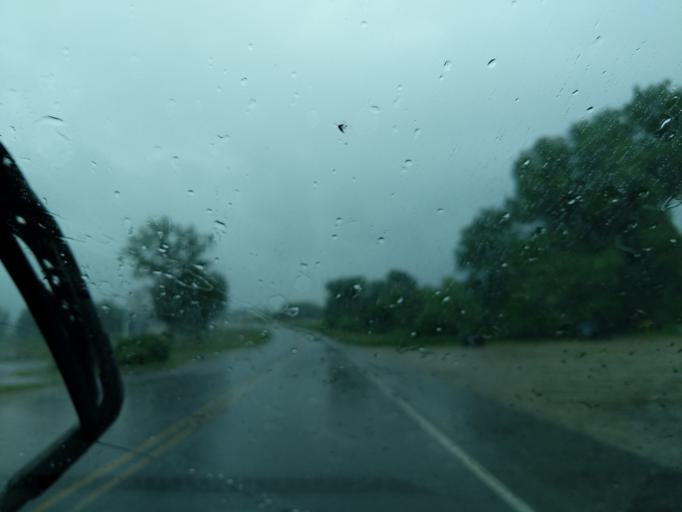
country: US
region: Michigan
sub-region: Berrien County
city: Coloma
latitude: 42.1747
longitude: -86.3058
